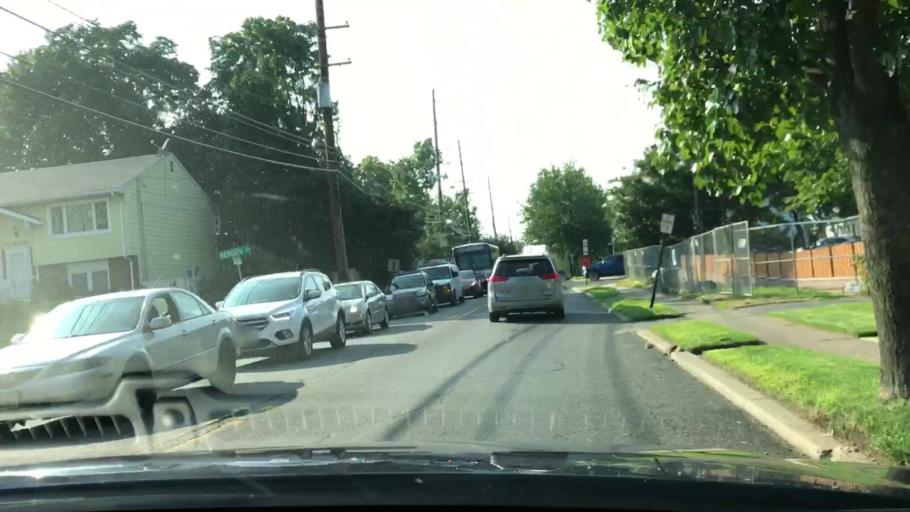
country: US
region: New Jersey
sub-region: Bergen County
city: Maywood
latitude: 40.9040
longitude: -74.0640
